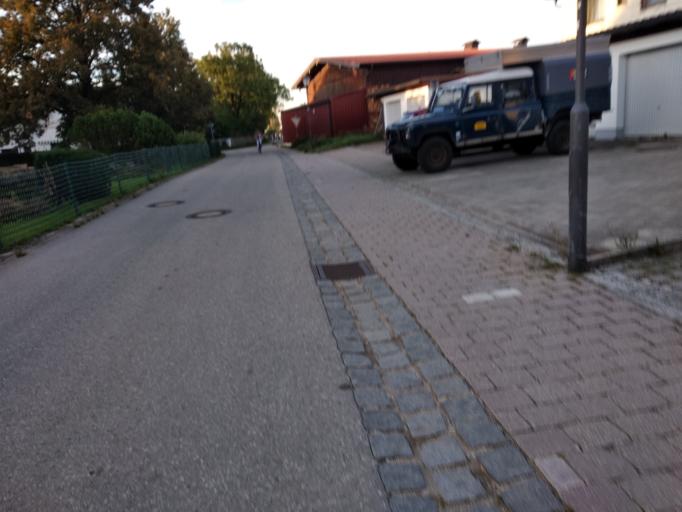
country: DE
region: Bavaria
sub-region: Upper Bavaria
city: Zorneding
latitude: 48.0820
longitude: 11.8190
